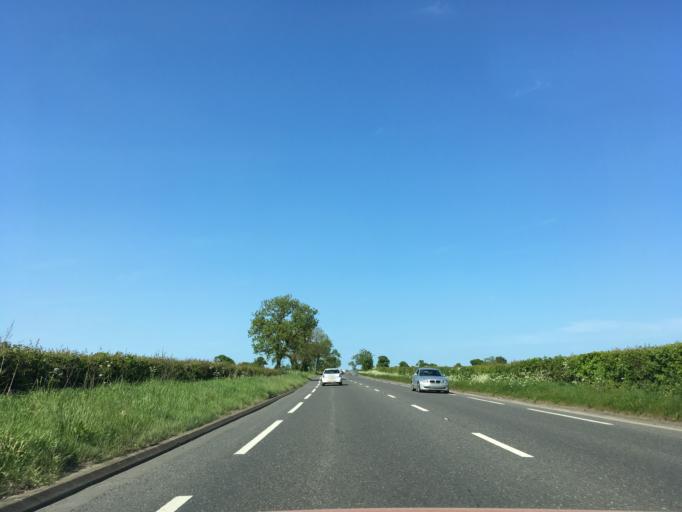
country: GB
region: England
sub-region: Gloucestershire
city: Dursley
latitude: 51.7469
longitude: -2.3491
